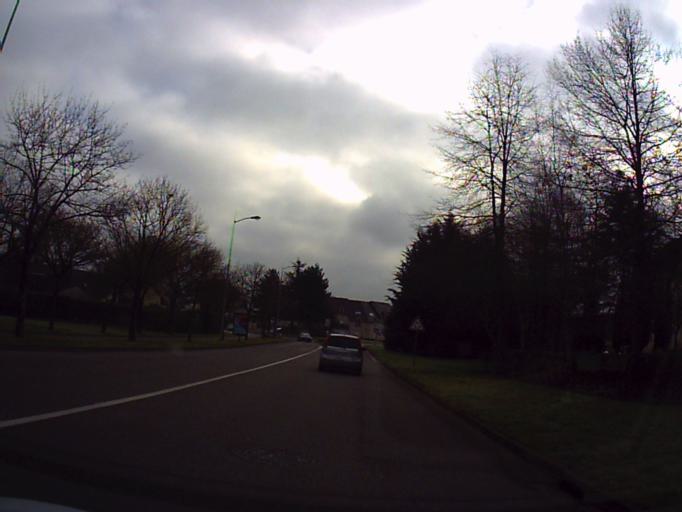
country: FR
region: Brittany
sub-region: Departement du Morbihan
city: Vannes
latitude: 47.6415
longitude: -2.7728
